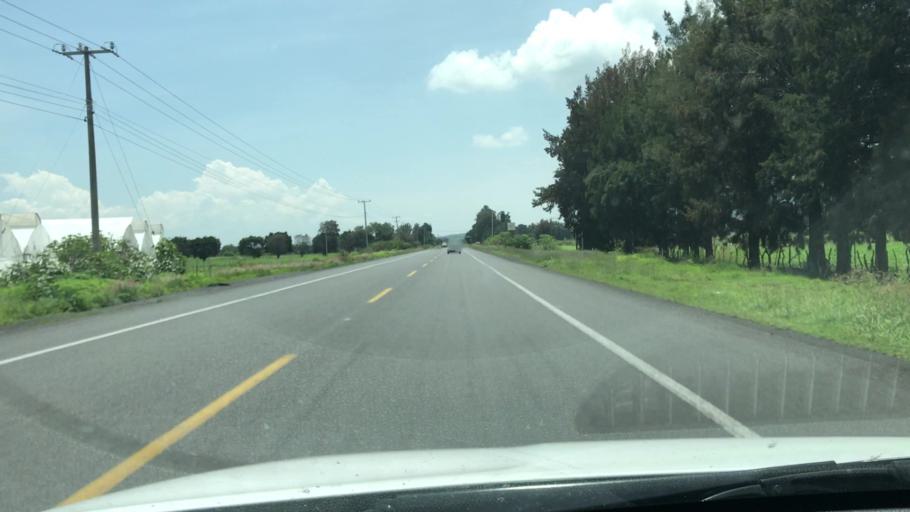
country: MX
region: Michoacan
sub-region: Yurecuaro
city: Yurecuaro
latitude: 20.3393
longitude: -102.1809
